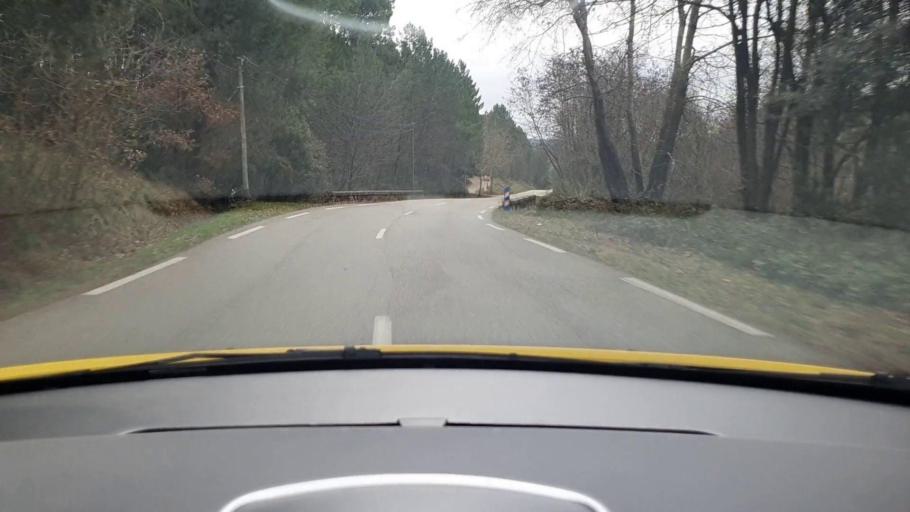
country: FR
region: Languedoc-Roussillon
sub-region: Departement du Gard
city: Les Salles-du-Gardon
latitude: 44.2560
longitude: 4.0459
